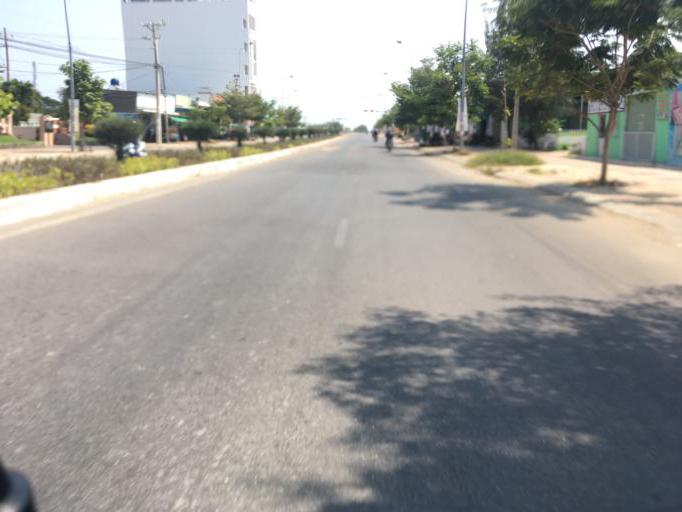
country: VN
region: Ninh Thuan
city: Phan Rang-Thap Cham
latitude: 11.5614
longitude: 109.0214
